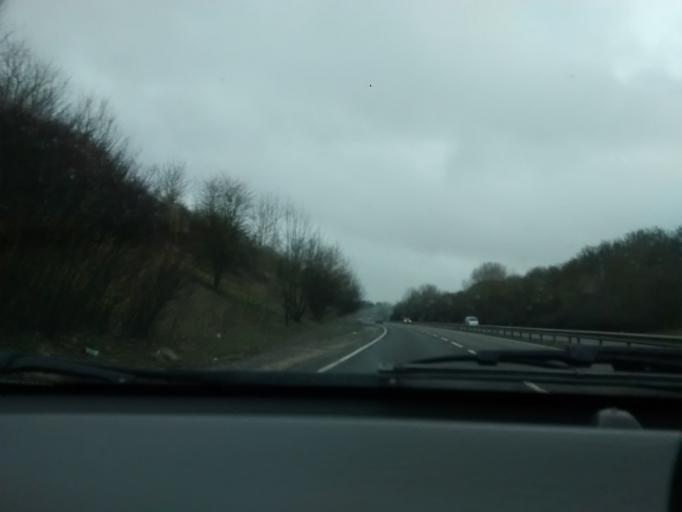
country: GB
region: England
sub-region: Suffolk
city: Needham Market
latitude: 52.1765
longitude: 1.0490
